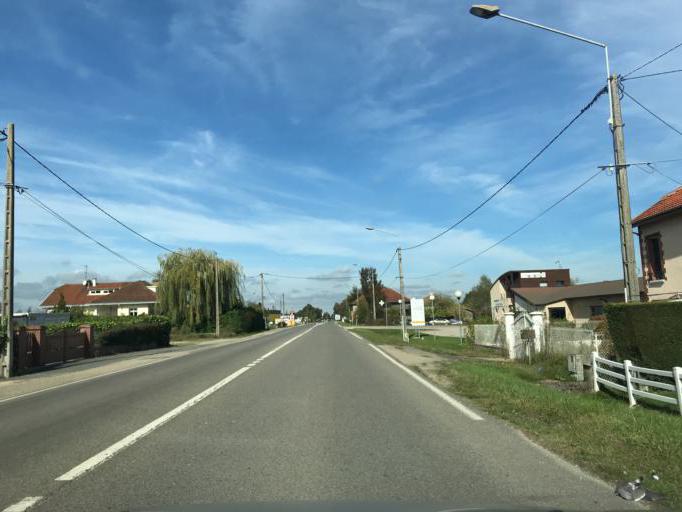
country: FR
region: Rhone-Alpes
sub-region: Departement de l'Ain
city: Montrevel-en-Bresse
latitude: 46.3432
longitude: 5.1270
